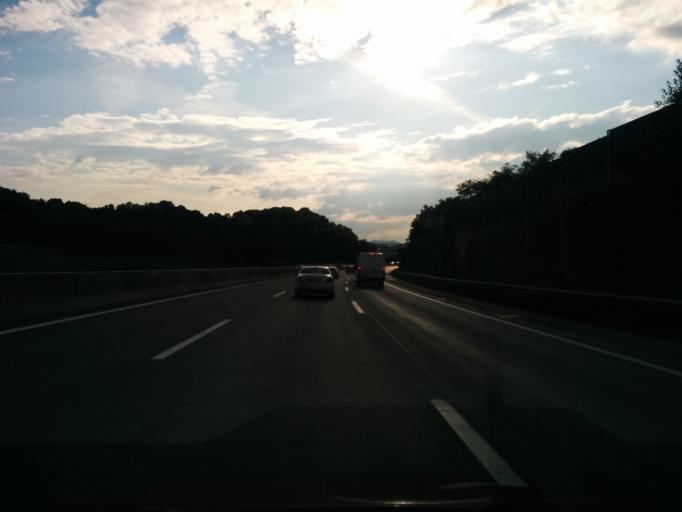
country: AT
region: Lower Austria
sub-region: Politischer Bezirk Melk
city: Melk
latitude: 48.2139
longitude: 15.3118
